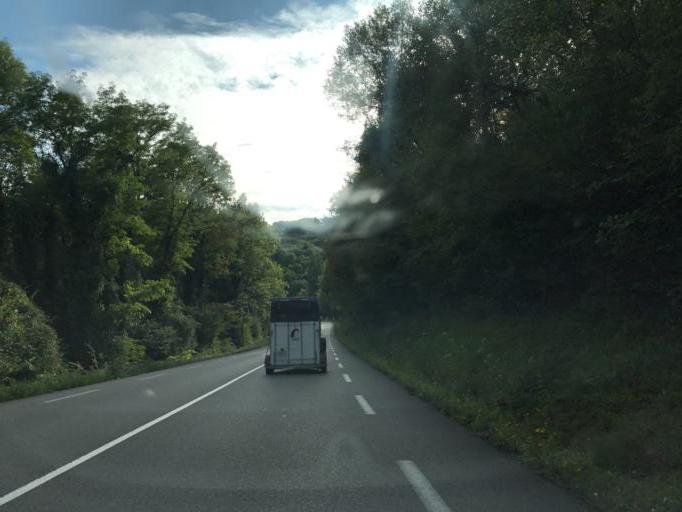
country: FR
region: Rhone-Alpes
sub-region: Departement de l'Ain
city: Collonges
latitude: 46.1045
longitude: 5.8771
